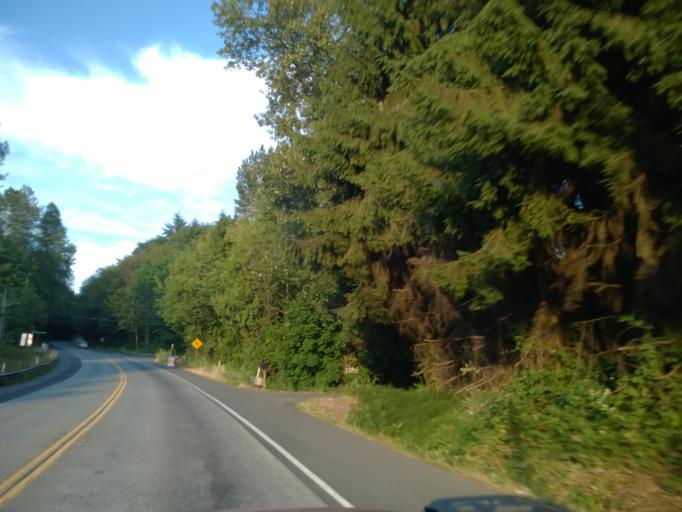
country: US
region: Washington
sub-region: King County
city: Redmond
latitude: 47.7113
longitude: -122.1227
